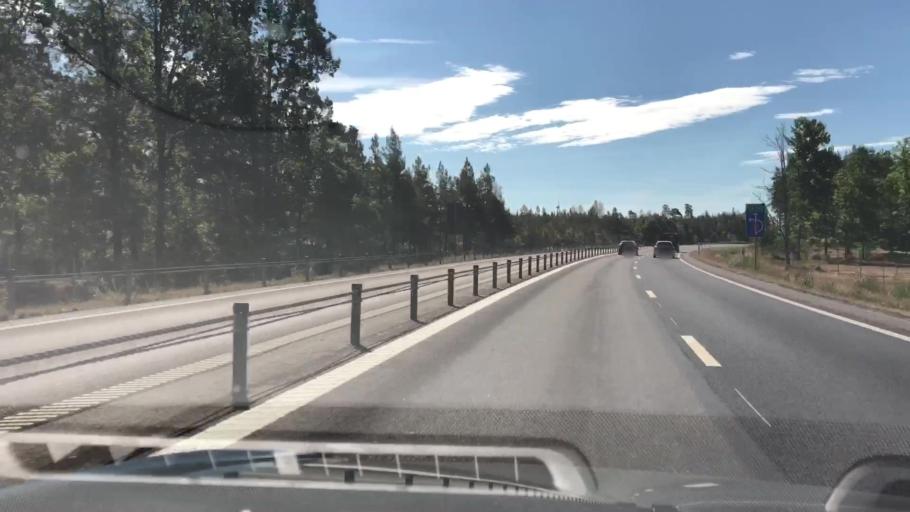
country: SE
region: Kalmar
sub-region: Oskarshamns Kommun
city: Paskallavik
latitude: 57.1149
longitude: 16.4985
